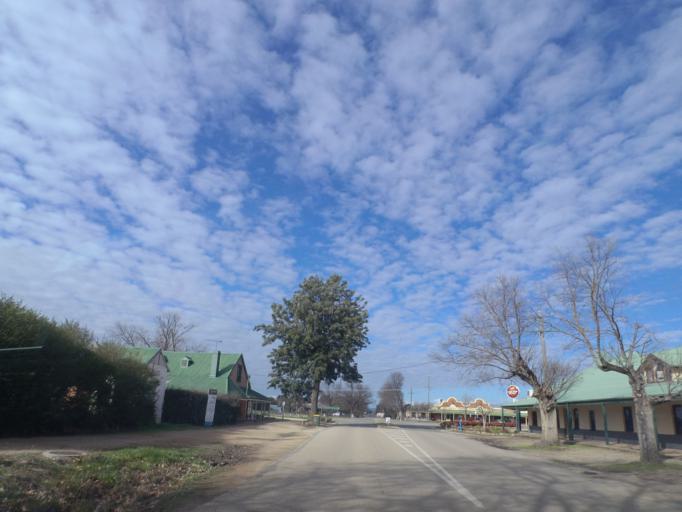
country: AU
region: Victoria
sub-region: Wangaratta
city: Wangaratta
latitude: -36.4489
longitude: 146.4315
